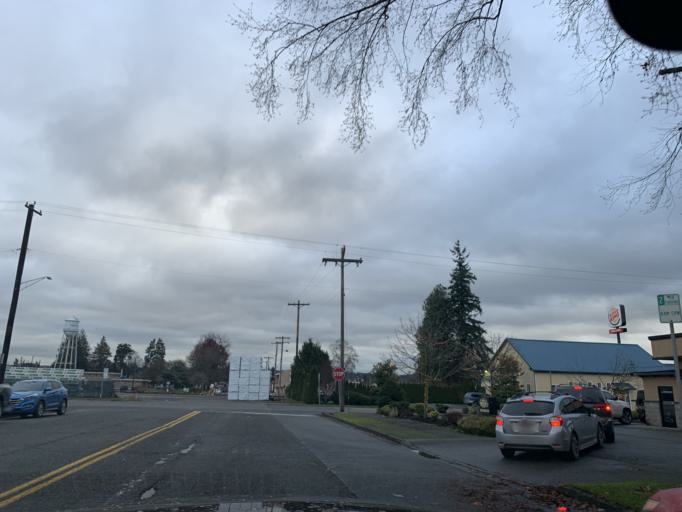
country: US
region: Washington
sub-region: Snohomish County
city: Marysville
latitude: 48.0528
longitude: -122.1811
